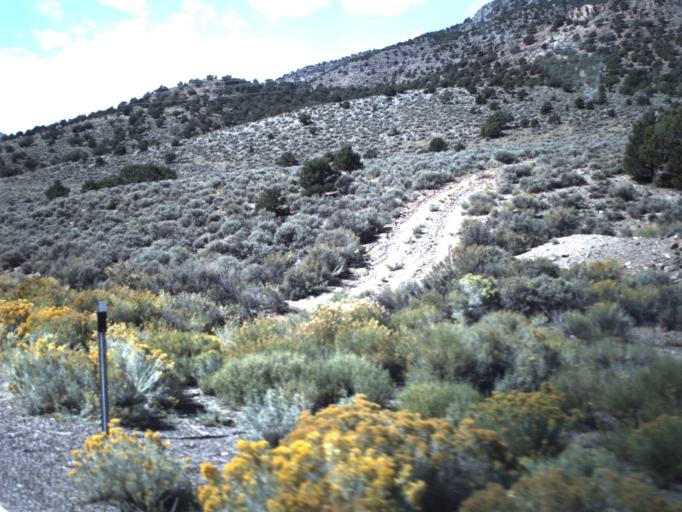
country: US
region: Utah
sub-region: Piute County
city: Junction
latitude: 38.2599
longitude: -112.2609
